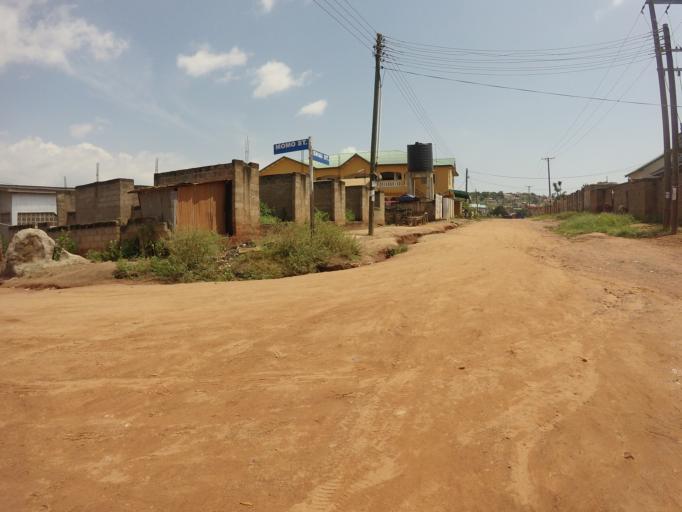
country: GH
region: Greater Accra
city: Gbawe
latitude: 5.6173
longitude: -0.3134
